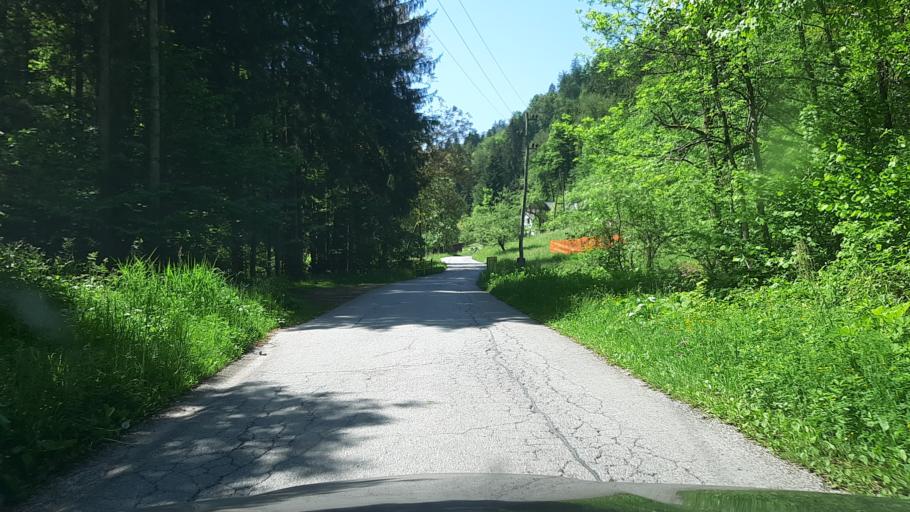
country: SI
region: Skofja Loka
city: Skofja Loka
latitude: 46.1399
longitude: 14.2958
